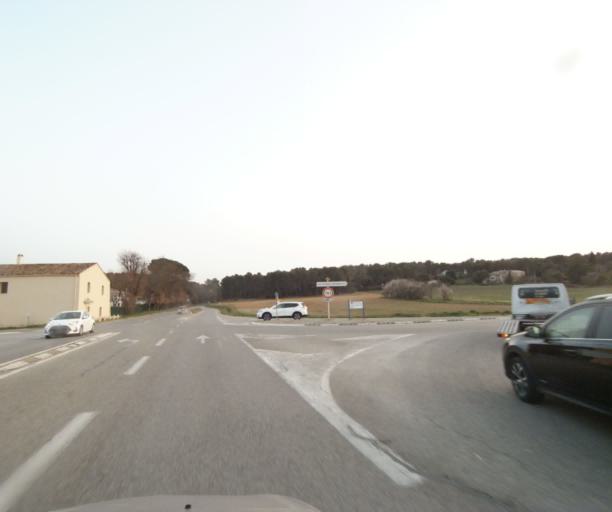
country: FR
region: Provence-Alpes-Cote d'Azur
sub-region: Departement des Bouches-du-Rhone
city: Cabries
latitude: 43.4403
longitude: 5.3615
